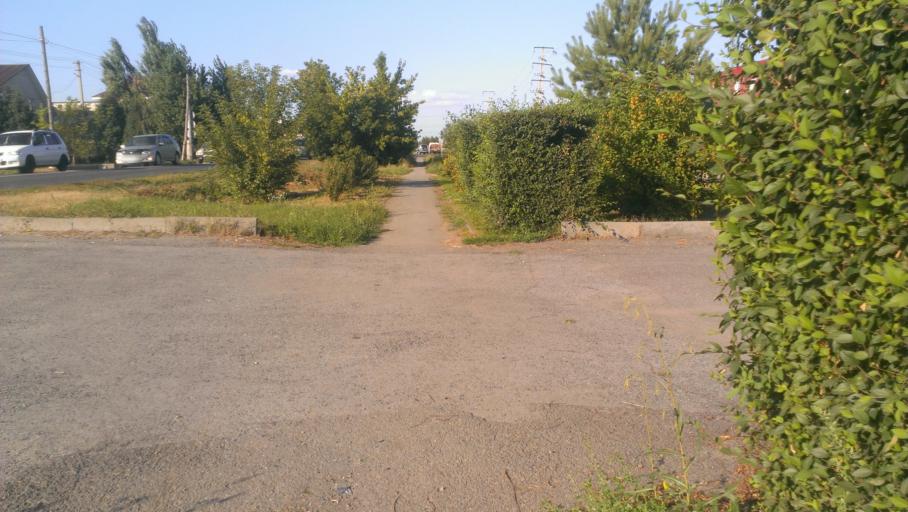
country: RU
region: Altai Krai
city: Novosilikatnyy
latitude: 53.3559
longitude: 83.6363
